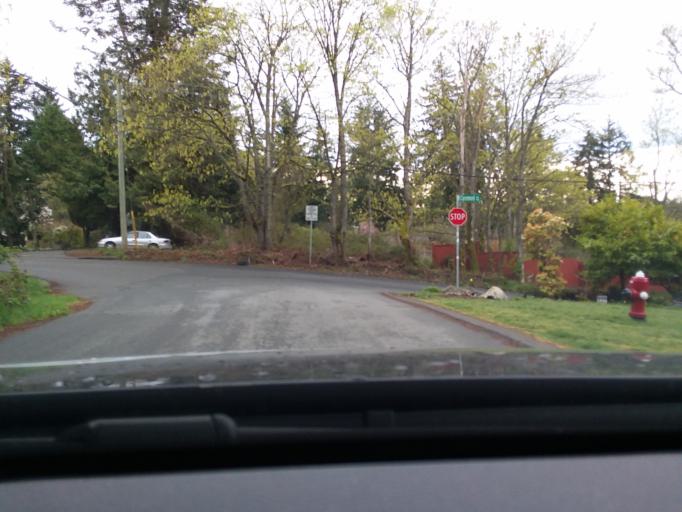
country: CA
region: British Columbia
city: Victoria
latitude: 48.5183
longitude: -123.3825
